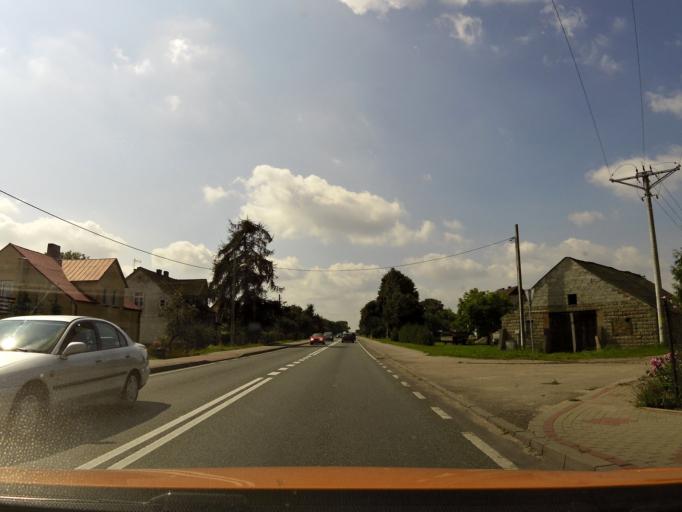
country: PL
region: West Pomeranian Voivodeship
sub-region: Powiat goleniowski
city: Nowogard
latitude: 53.7177
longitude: 15.1890
